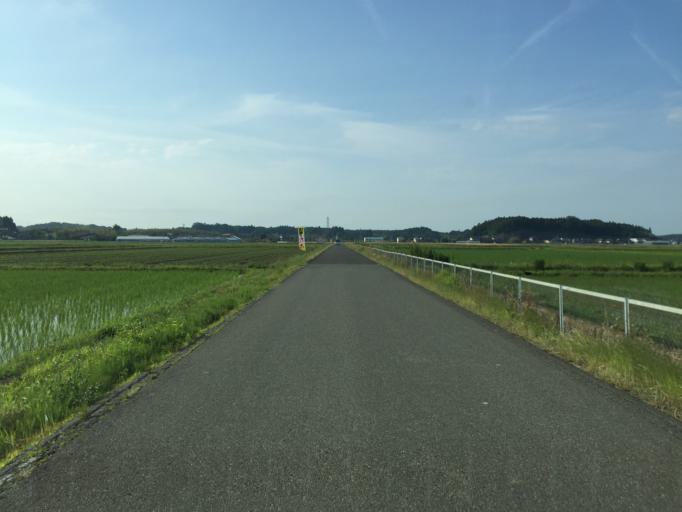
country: JP
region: Miyagi
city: Marumori
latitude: 37.7976
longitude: 140.9488
